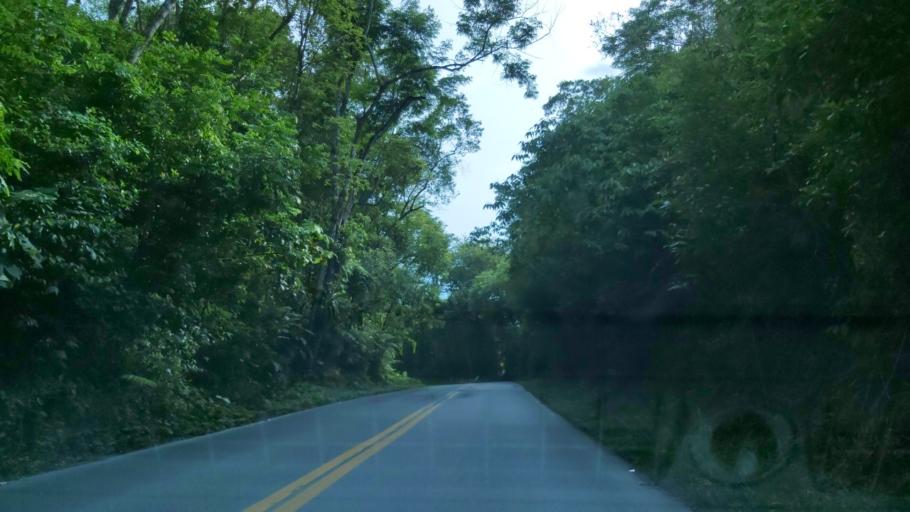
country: BR
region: Sao Paulo
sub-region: Juquia
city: Juquia
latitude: -24.1019
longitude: -47.6264
